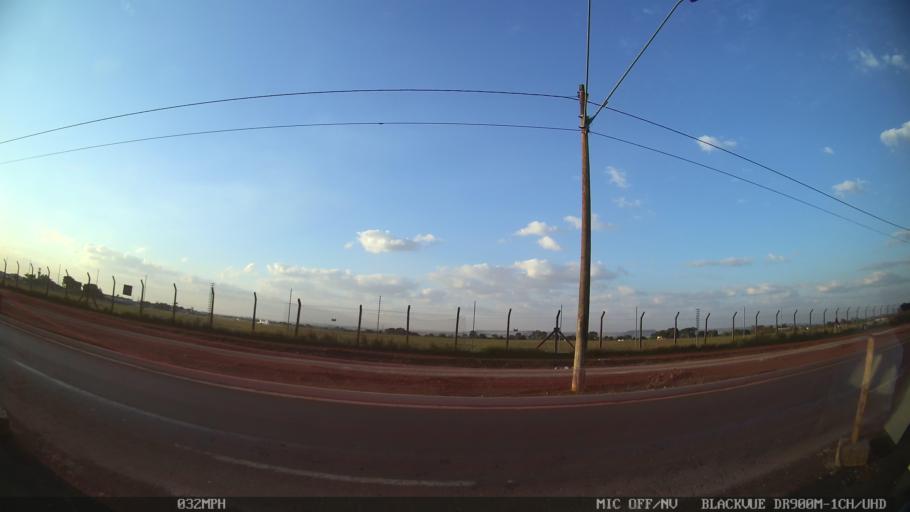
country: BR
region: Sao Paulo
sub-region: Ribeirao Preto
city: Ribeirao Preto
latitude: -21.1441
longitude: -47.7746
